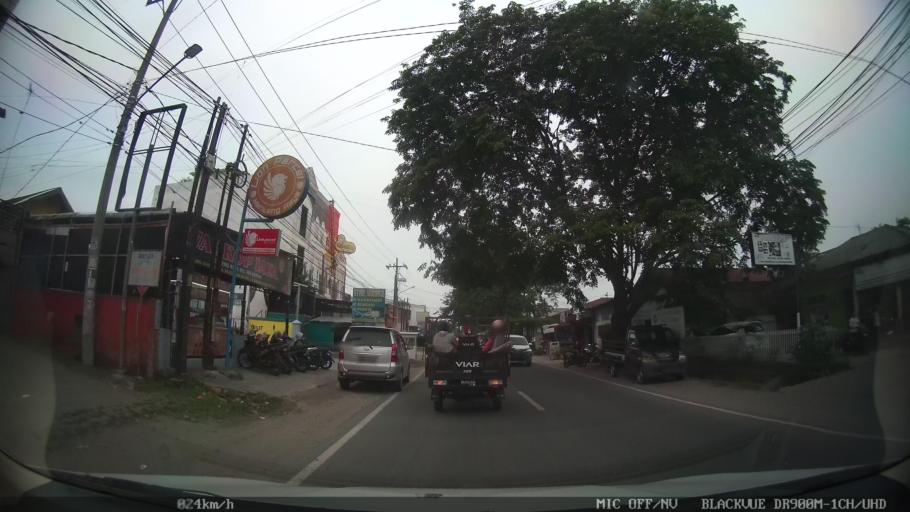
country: ID
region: North Sumatra
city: Medan
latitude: 3.5682
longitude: 98.7168
